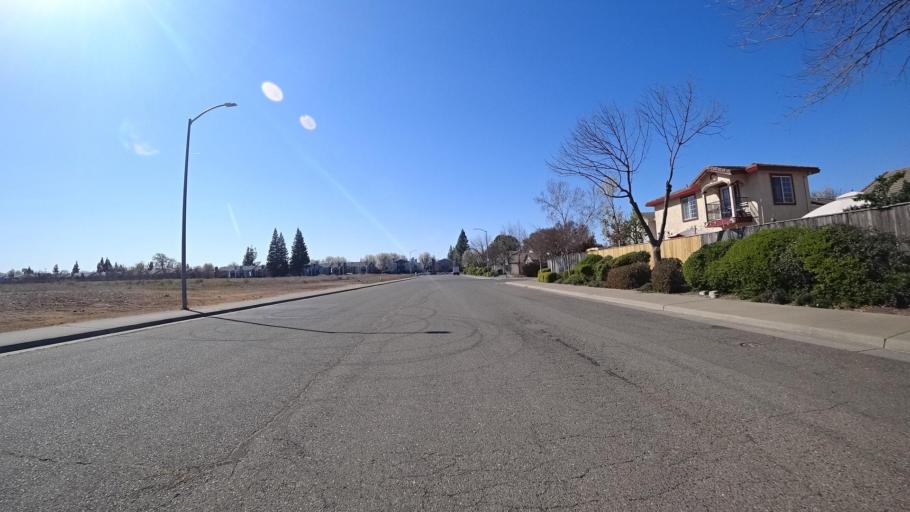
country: US
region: California
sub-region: Sacramento County
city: Rancho Cordova
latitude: 38.5785
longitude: -121.2932
